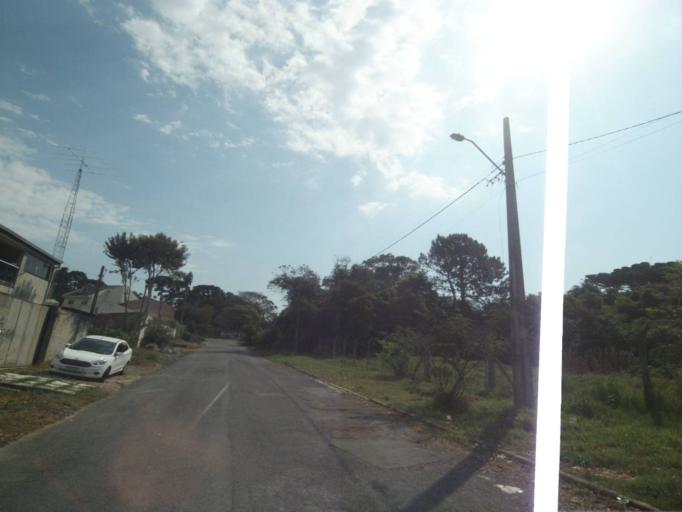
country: BR
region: Parana
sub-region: Sao Jose Dos Pinhais
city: Sao Jose dos Pinhais
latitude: -25.5158
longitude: -49.2518
